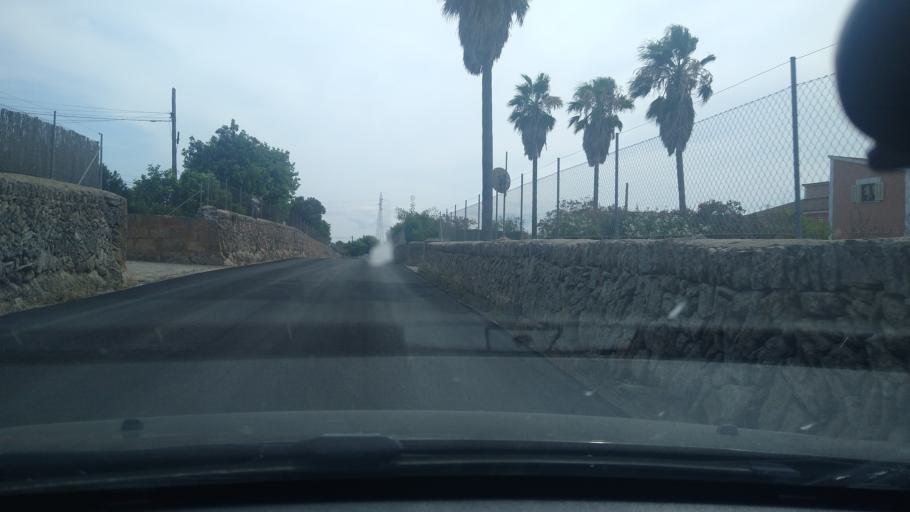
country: ES
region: Balearic Islands
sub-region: Illes Balears
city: Santa Margalida
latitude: 39.7291
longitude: 3.1173
